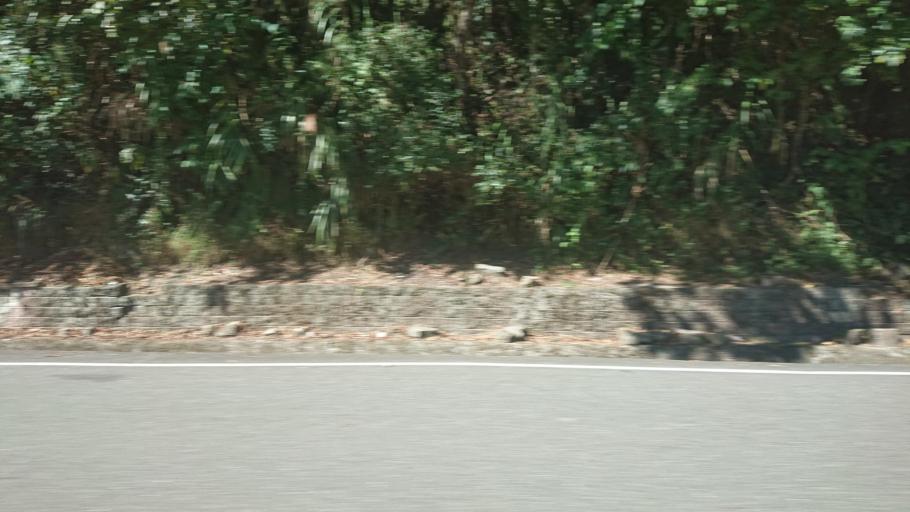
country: TW
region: Taiwan
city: Lugu
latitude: 23.4811
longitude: 120.7350
